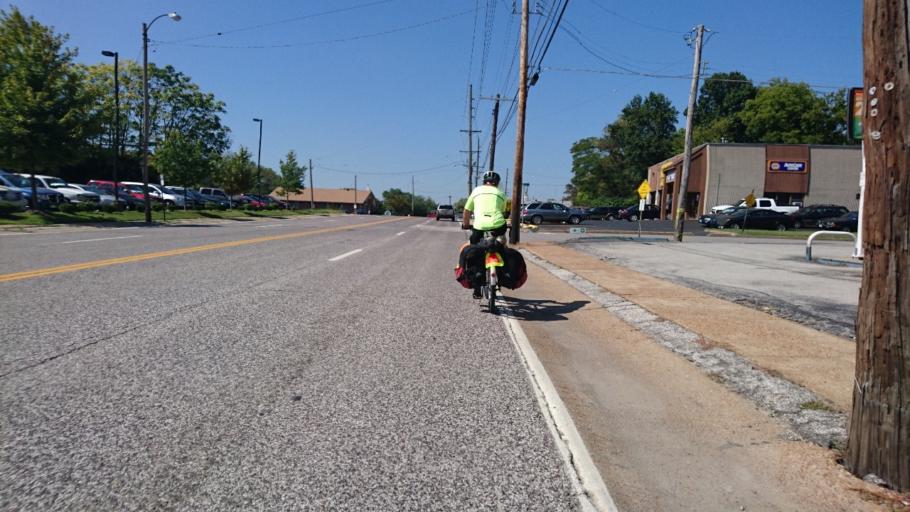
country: US
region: Missouri
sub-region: Saint Louis County
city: Brentwood
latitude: 38.6118
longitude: -90.3387
